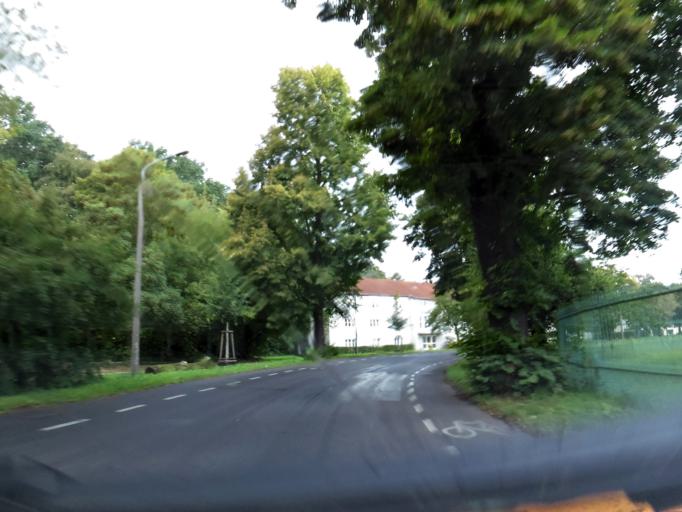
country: DE
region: Brandenburg
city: Potsdam
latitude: 52.3991
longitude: 13.0117
